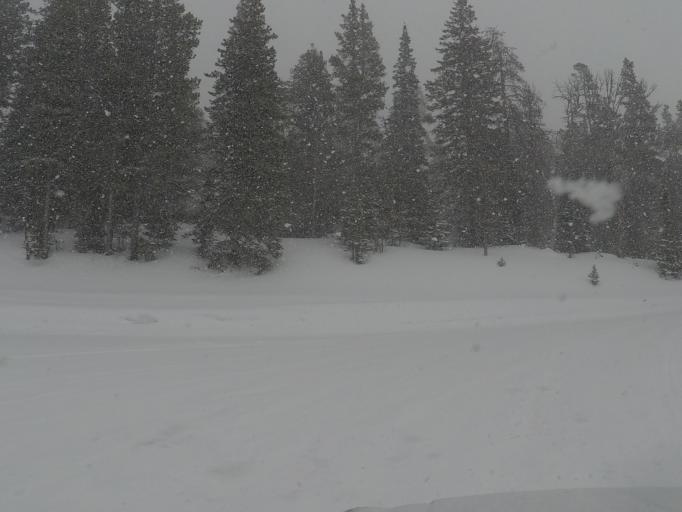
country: US
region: Montana
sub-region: Meagher County
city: White Sulphur Springs
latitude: 46.8389
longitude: -110.6976
